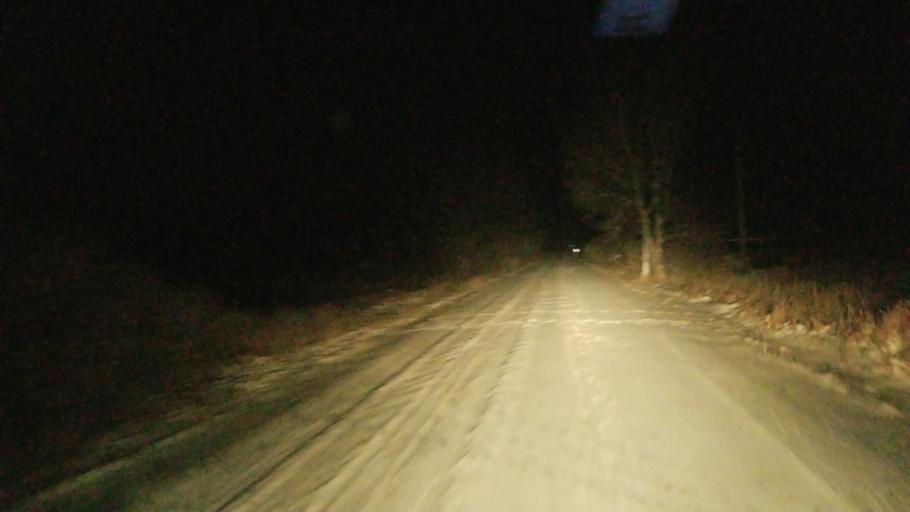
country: US
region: Michigan
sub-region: Osceola County
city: Reed City
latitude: 43.8337
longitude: -85.4141
